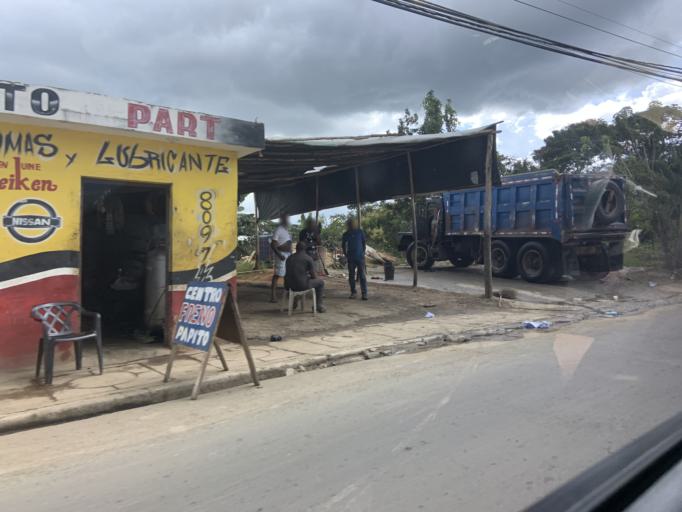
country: DO
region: Monte Plata
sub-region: Yamasa
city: Yamasa
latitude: 18.7782
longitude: -70.0259
